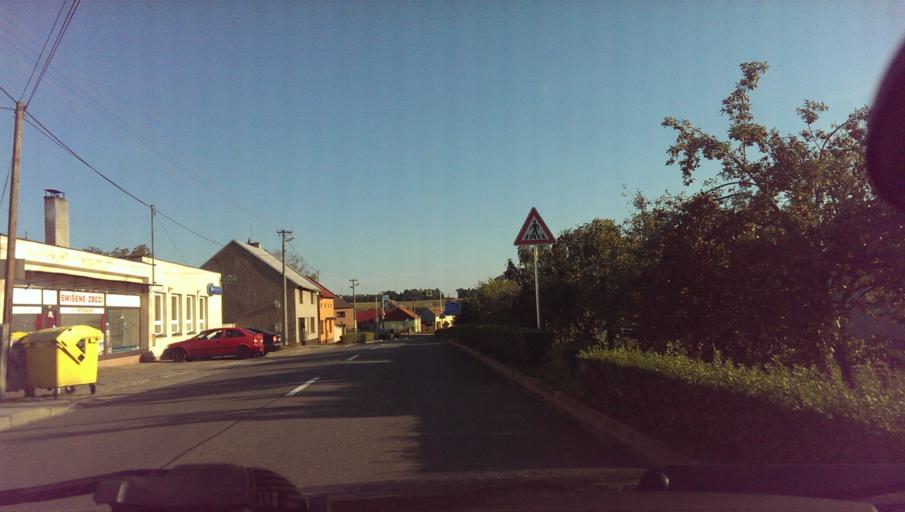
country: CZ
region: Zlin
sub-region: Okres Zlin
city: Otrokovice
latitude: 49.2517
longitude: 17.5427
